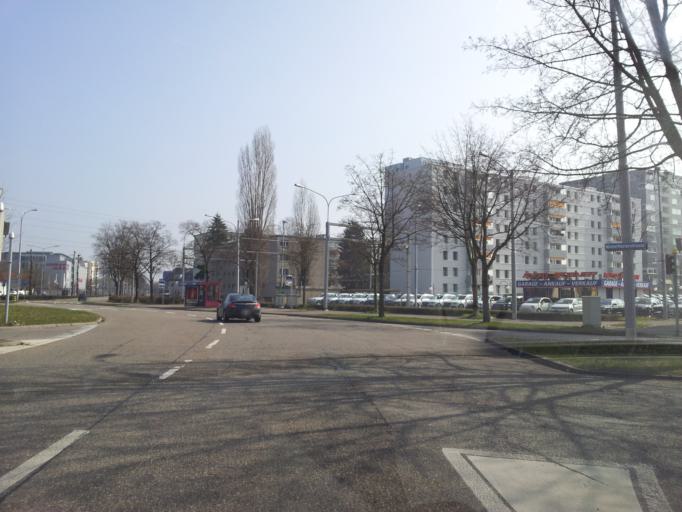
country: CH
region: Zurich
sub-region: Bezirk Zuerich
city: Zuerich (Kreis 12) / Hirzenbach
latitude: 47.4072
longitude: 8.5856
